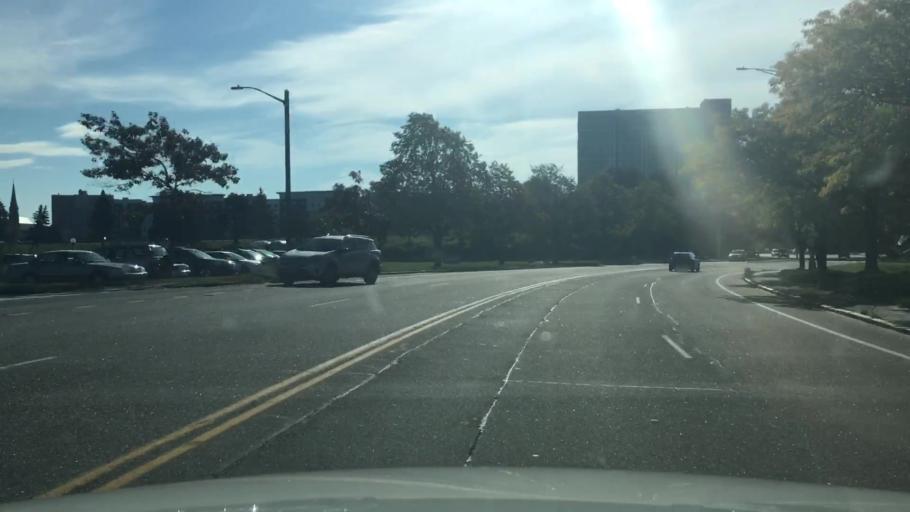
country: US
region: Maine
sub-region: Cumberland County
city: Portland
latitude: 43.6644
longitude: -70.2673
